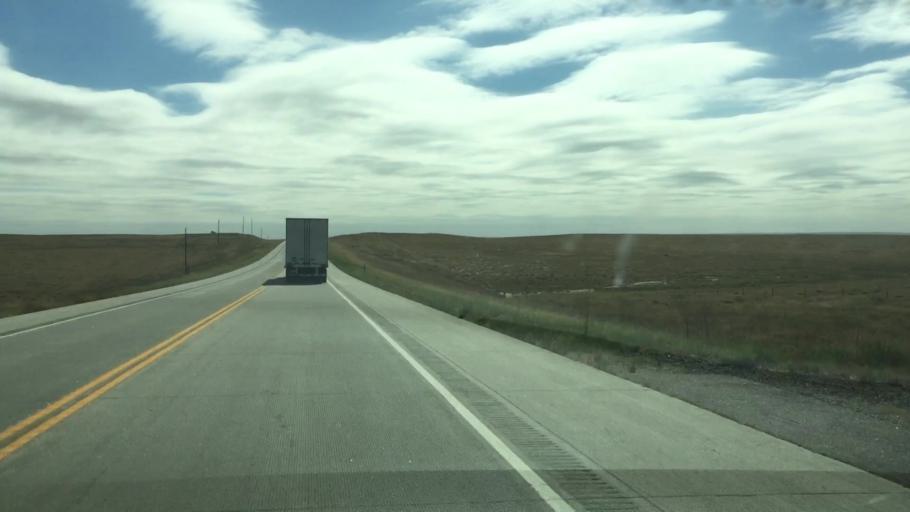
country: US
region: Colorado
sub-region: Lincoln County
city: Hugo
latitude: 39.0063
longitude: -103.2933
